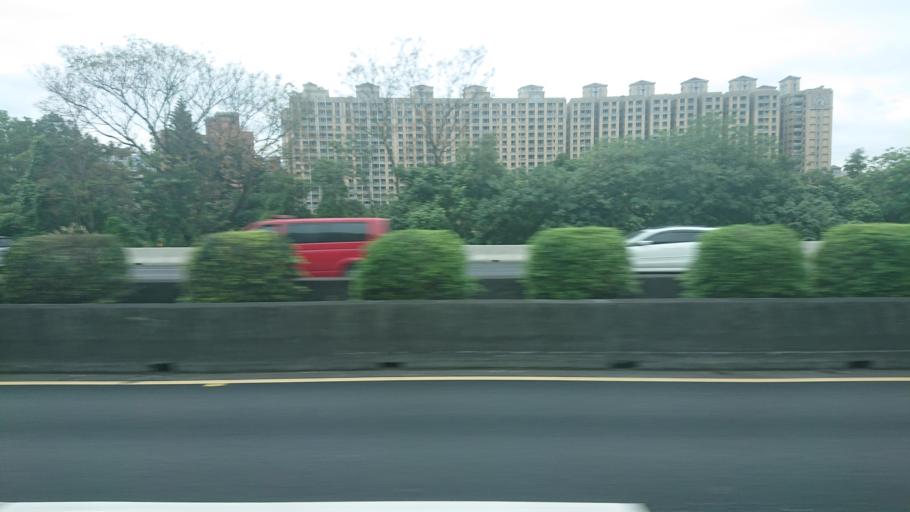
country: TW
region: Taipei
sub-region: Taipei
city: Banqiao
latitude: 24.9506
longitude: 121.4139
